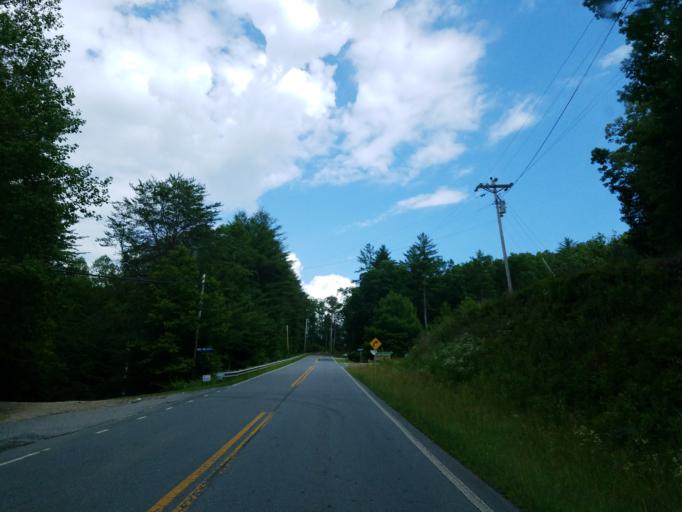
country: US
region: Georgia
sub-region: Fannin County
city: Blue Ridge
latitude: 34.7887
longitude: -84.2697
